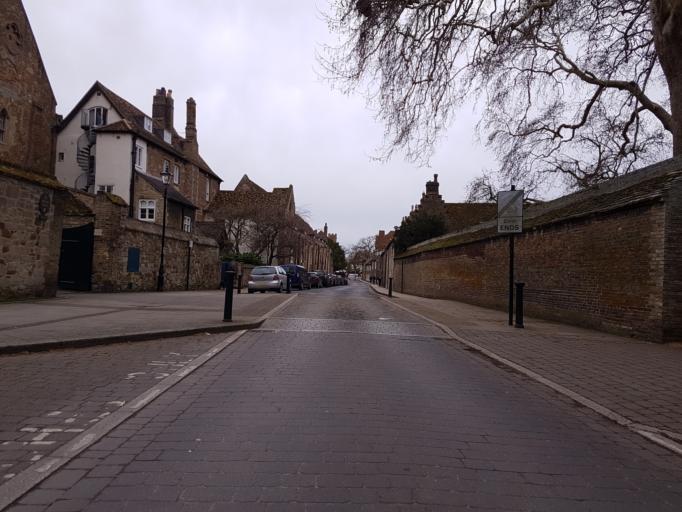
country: GB
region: England
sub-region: Cambridgeshire
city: Ely
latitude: 52.3983
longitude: 0.2623
